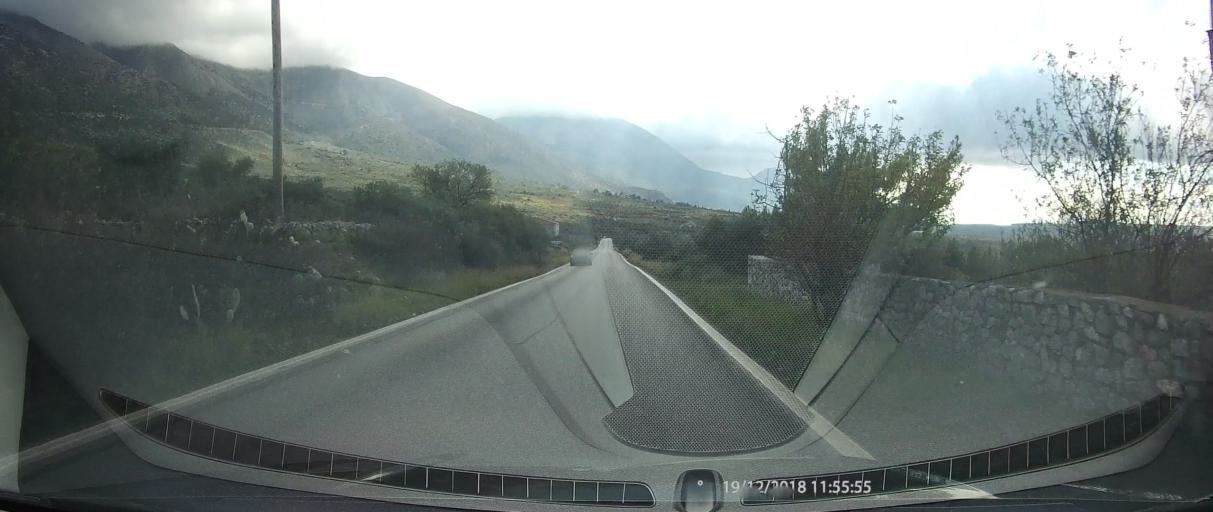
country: GR
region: Peloponnese
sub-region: Nomos Lakonias
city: Gytheio
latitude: 36.6045
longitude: 22.3974
